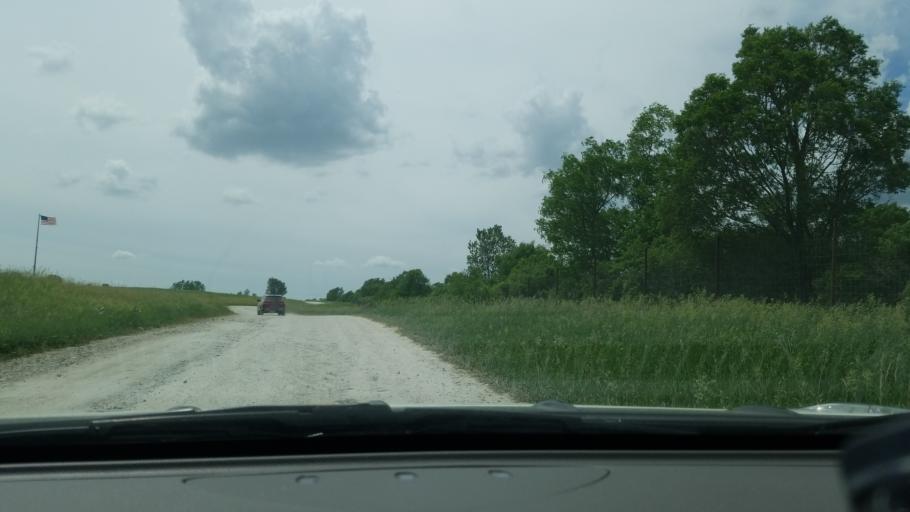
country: US
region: Nebraska
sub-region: Saunders County
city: Ashland
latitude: 41.0116
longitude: -96.2972
